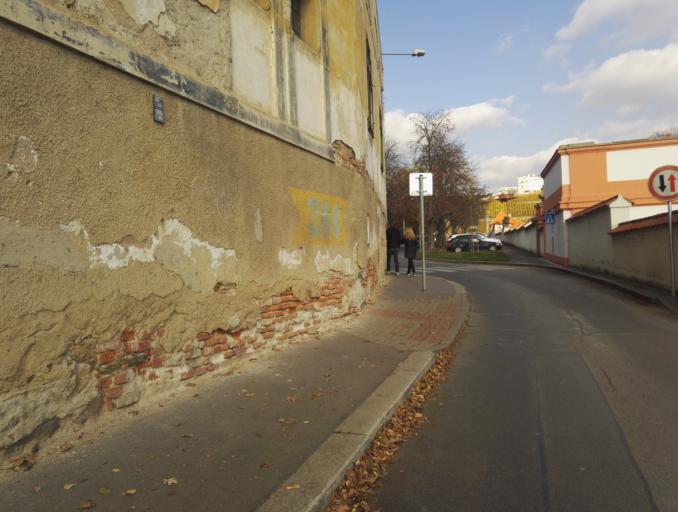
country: CZ
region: Praha
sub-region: Praha 1
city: Mala Strana
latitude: 50.1148
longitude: 14.4111
